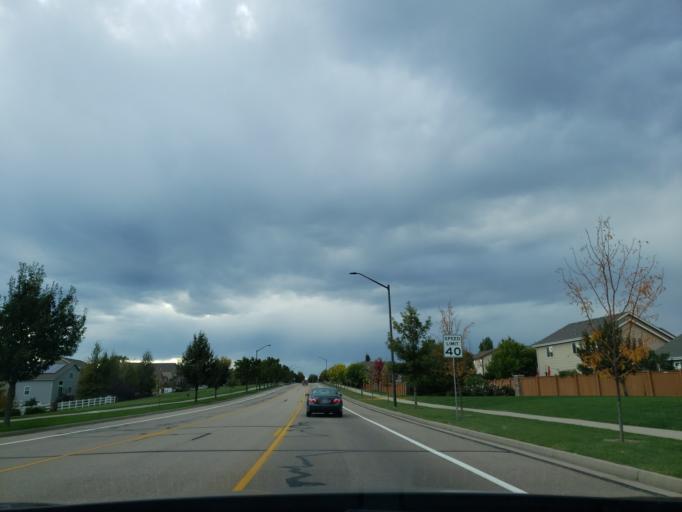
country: US
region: Colorado
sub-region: Larimer County
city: Fort Collins
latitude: 40.6248
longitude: -105.0343
